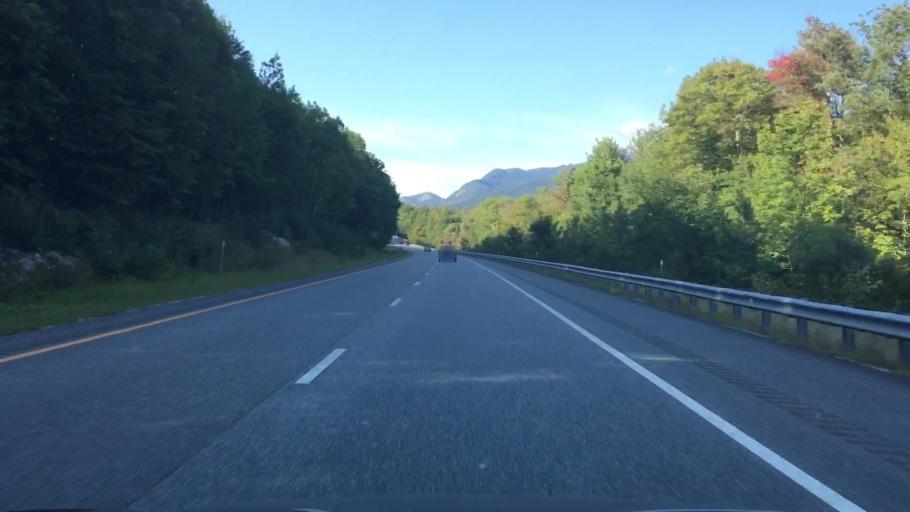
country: US
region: New Hampshire
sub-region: Grafton County
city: Woodstock
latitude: 44.0720
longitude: -71.6882
